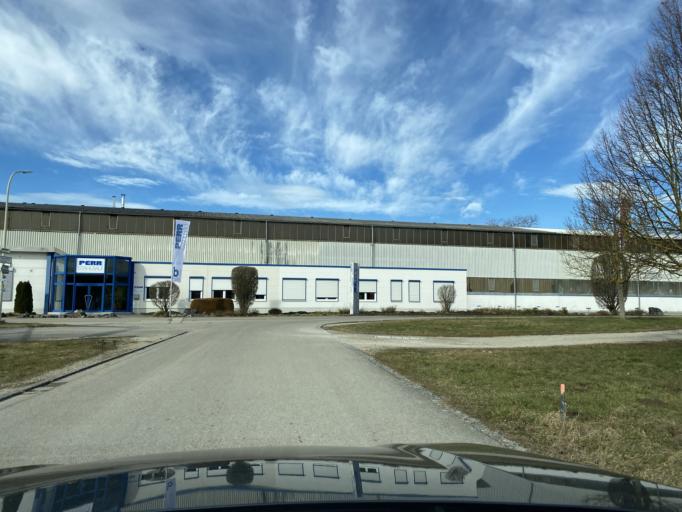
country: DE
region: Bavaria
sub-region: Upper Palatinate
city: Dietfurt
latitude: 49.0242
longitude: 11.5909
